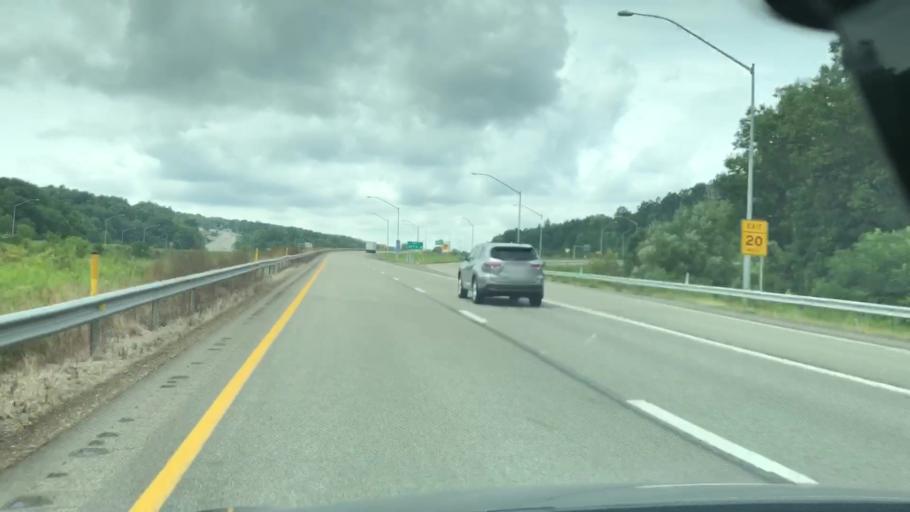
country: US
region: Pennsylvania
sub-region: Crawford County
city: Meadville
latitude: 41.6194
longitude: -80.1756
